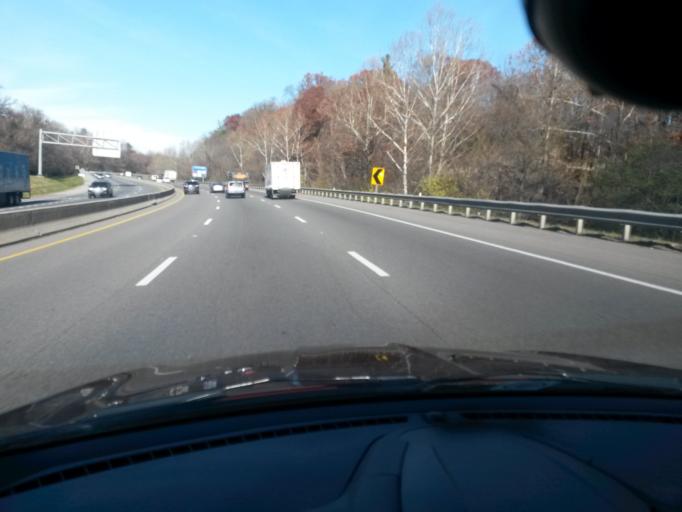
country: US
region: Virginia
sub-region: Roanoke County
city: Narrows
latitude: 37.2396
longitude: -79.9726
